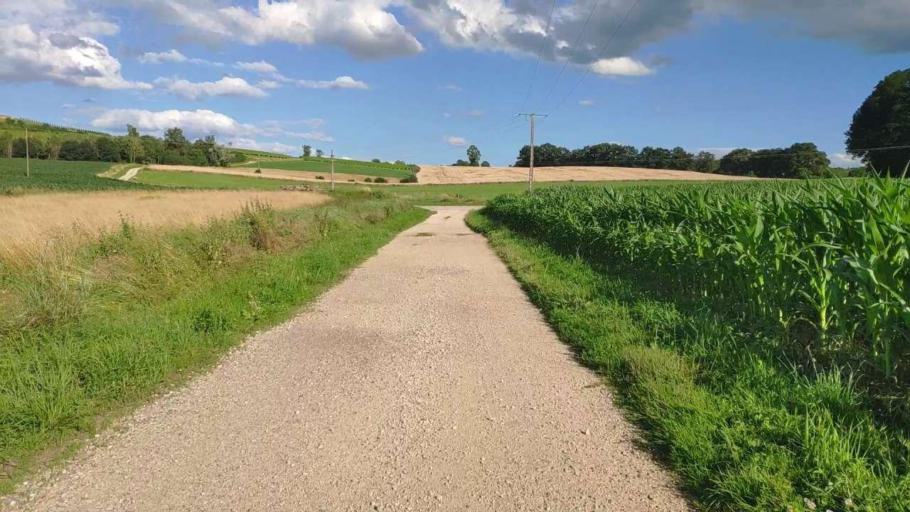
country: FR
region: Franche-Comte
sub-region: Departement du Jura
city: Bletterans
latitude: 46.7568
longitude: 5.5268
